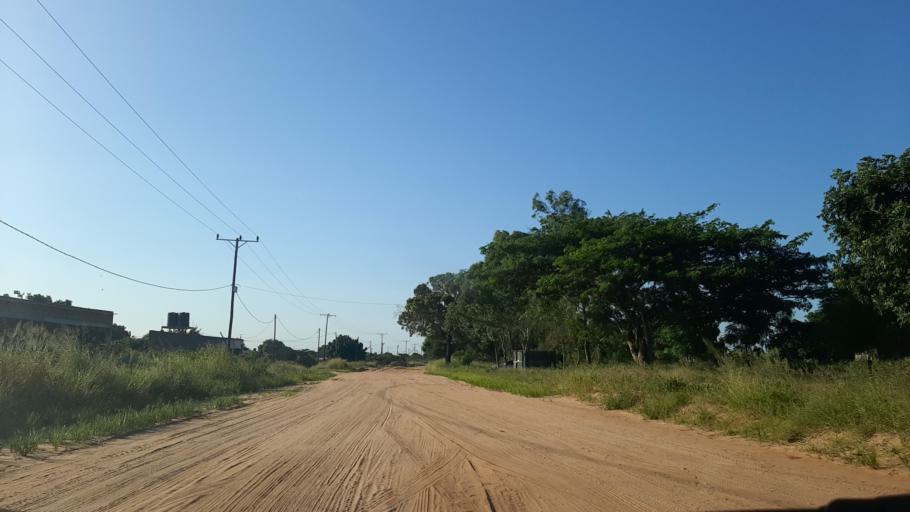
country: MZ
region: Maputo City
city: Maputo
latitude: -25.7705
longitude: 32.5487
